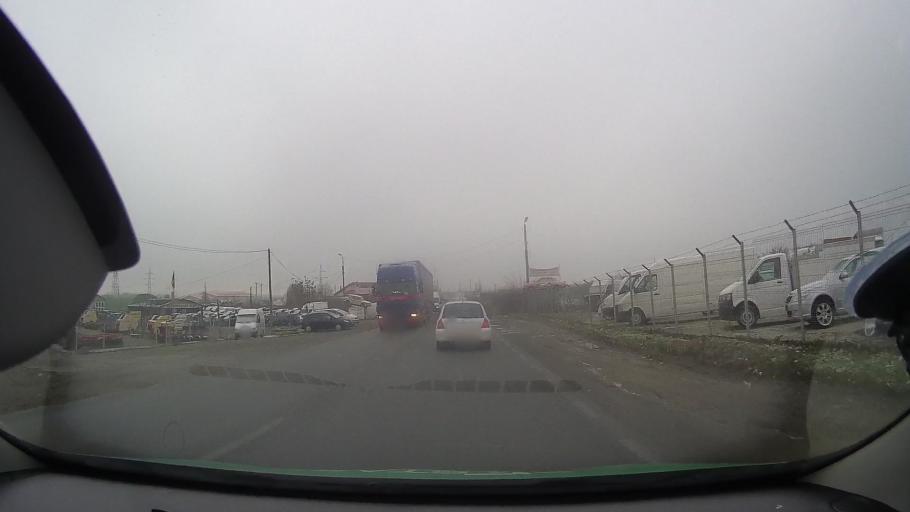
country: RO
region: Cluj
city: Turda
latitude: 46.5569
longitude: 23.7724
